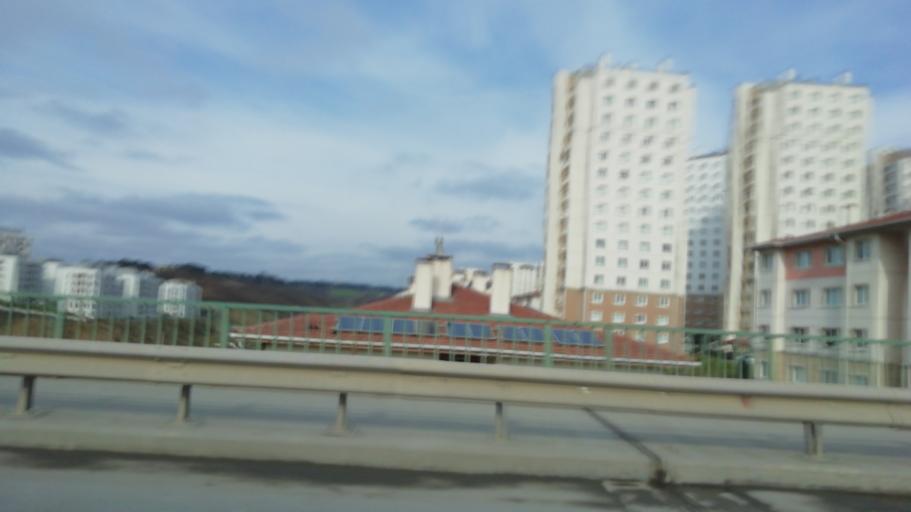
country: TR
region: Istanbul
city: Basaksehir
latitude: 41.1303
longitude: 28.7846
